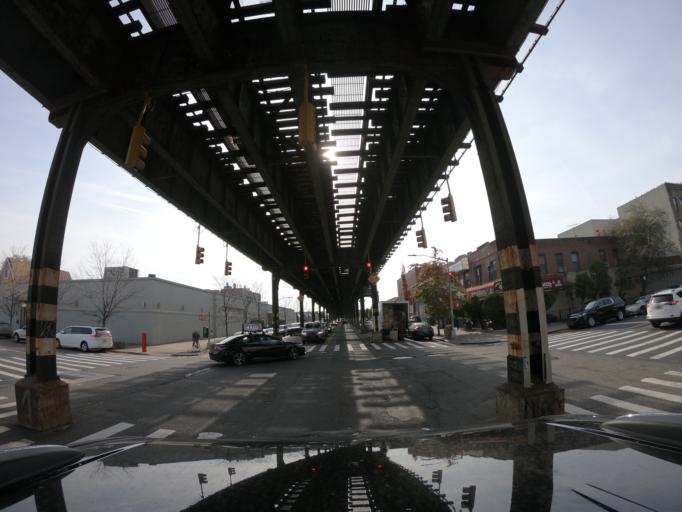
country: US
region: New York
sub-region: Kings County
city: Bensonhurst
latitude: 40.6137
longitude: -73.9739
